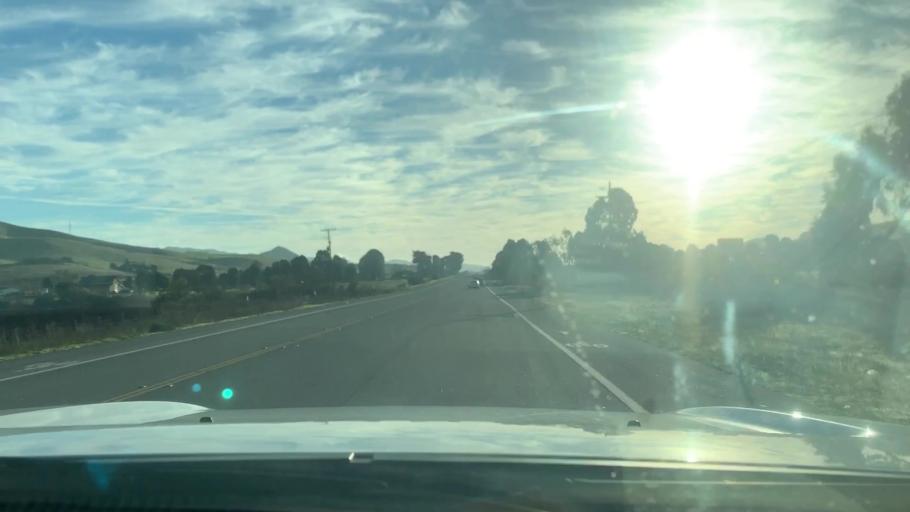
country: US
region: California
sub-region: San Luis Obispo County
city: Los Osos
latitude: 35.2947
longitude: -120.7606
